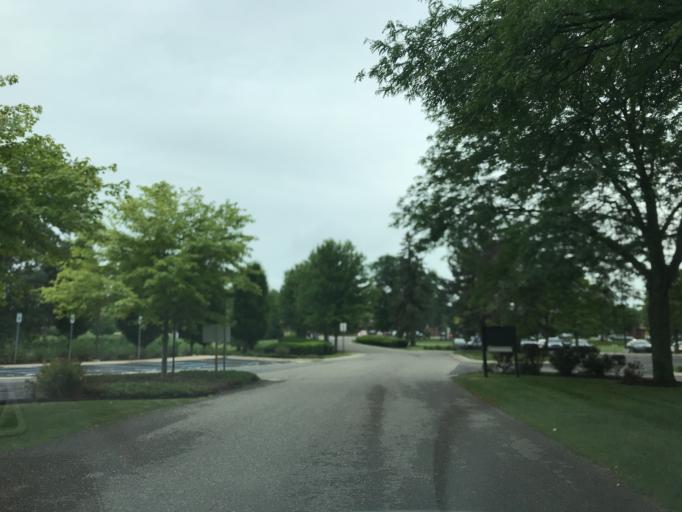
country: US
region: Michigan
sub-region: Oakland County
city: Farmington
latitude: 42.4703
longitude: -83.3888
